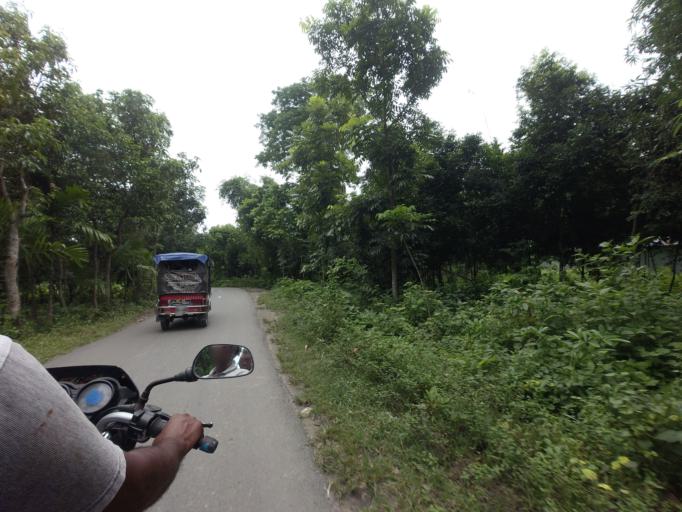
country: BD
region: Khulna
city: Kalia
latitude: 23.1298
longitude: 89.6443
